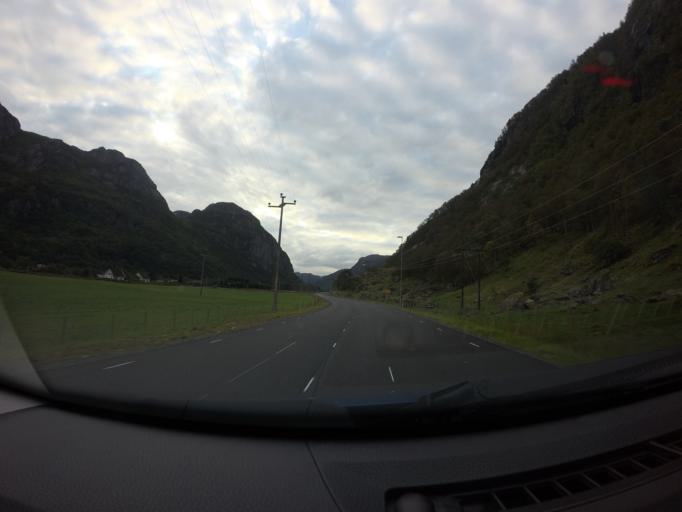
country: NO
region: Rogaland
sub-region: Forsand
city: Forsand
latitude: 58.8325
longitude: 6.1796
